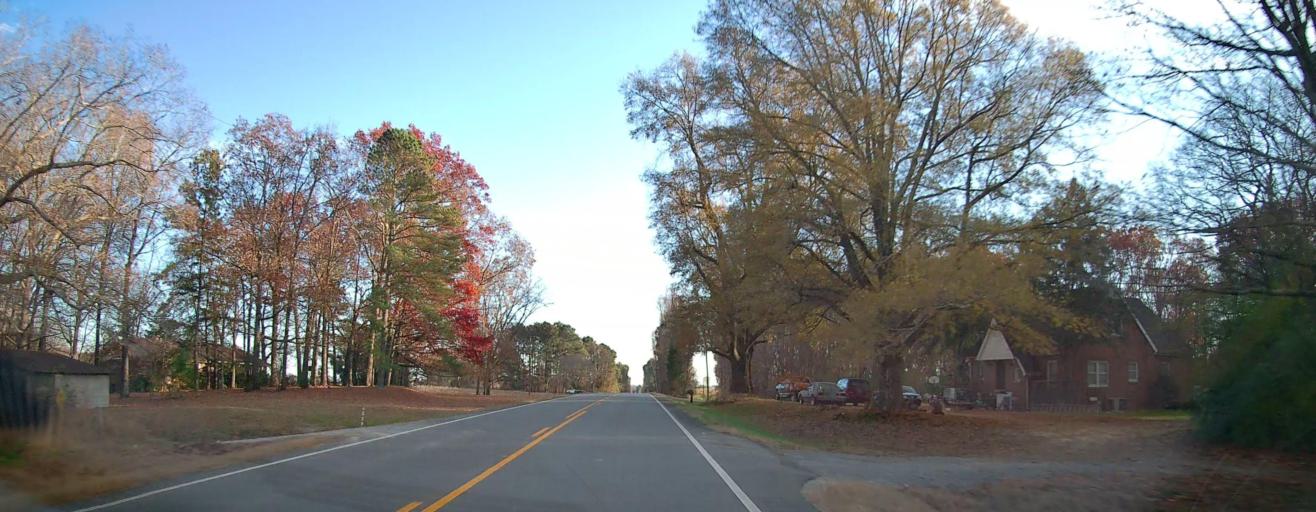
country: US
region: Alabama
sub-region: Marshall County
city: Arab
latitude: 34.2642
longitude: -86.5752
